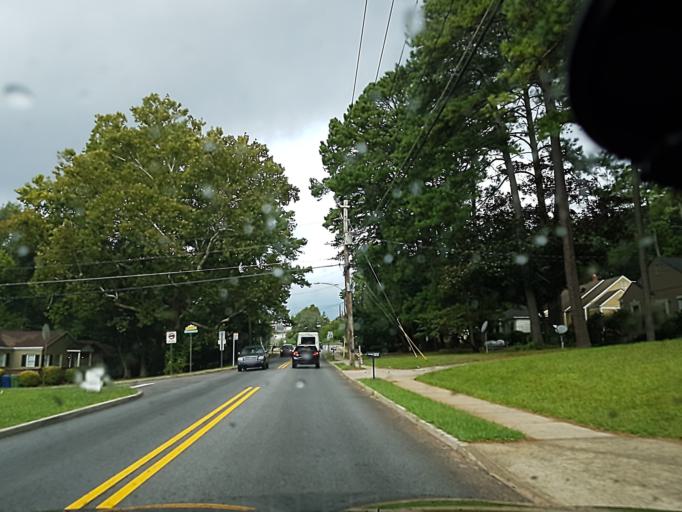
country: US
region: Georgia
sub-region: DeKalb County
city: North Druid Hills
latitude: 33.8199
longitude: -84.3561
